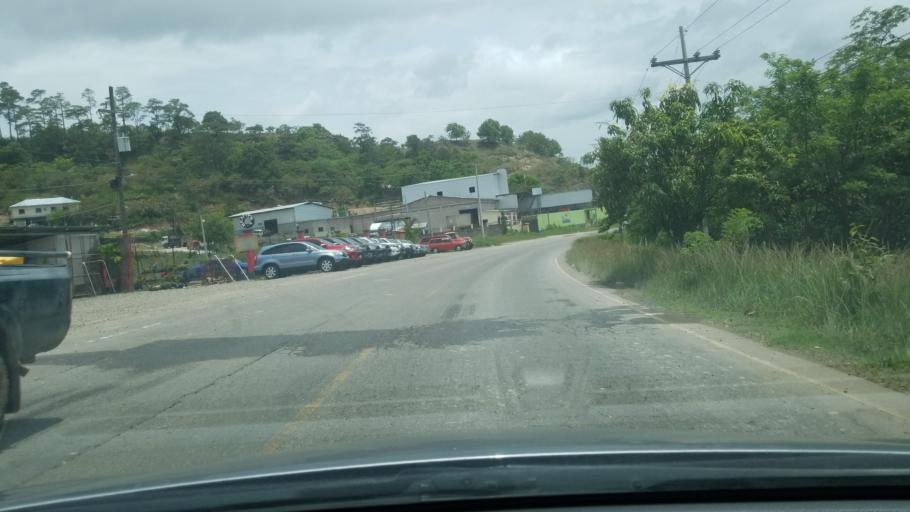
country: HN
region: Copan
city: Cucuyagua
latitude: 14.6696
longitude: -88.8567
